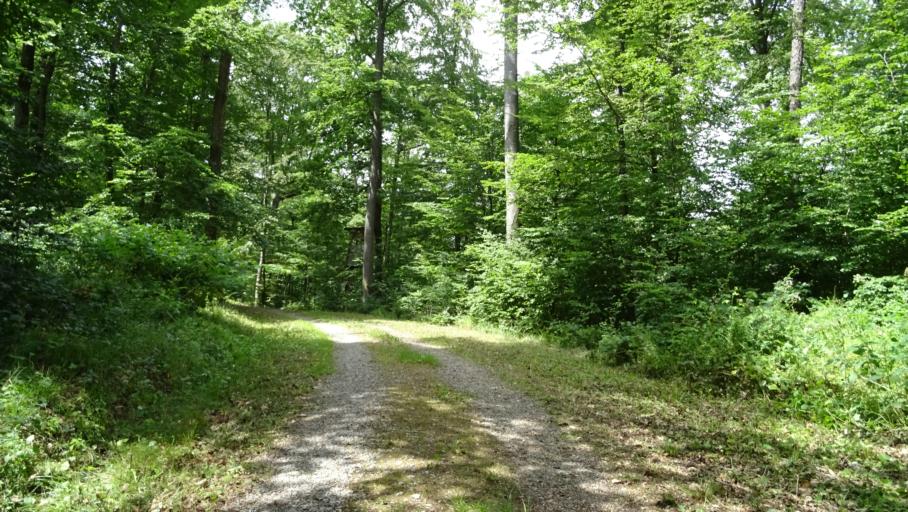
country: DE
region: Baden-Wuerttemberg
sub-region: Karlsruhe Region
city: Obrigheim
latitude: 49.3834
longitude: 9.1144
